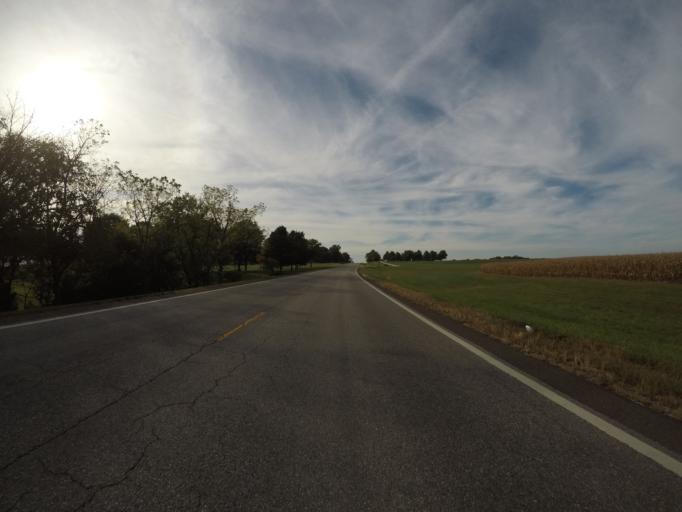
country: US
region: Kansas
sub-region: Douglas County
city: Baldwin City
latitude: 38.7687
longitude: -95.1530
